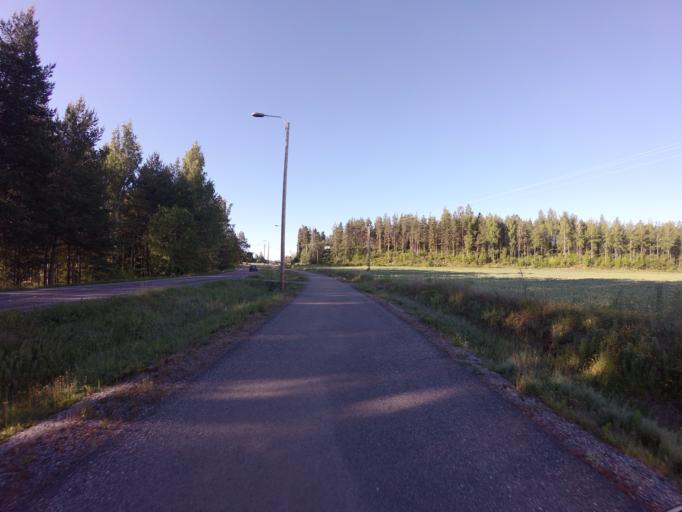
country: FI
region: Varsinais-Suomi
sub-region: Turku
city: Vahto
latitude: 60.5340
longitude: 22.3438
